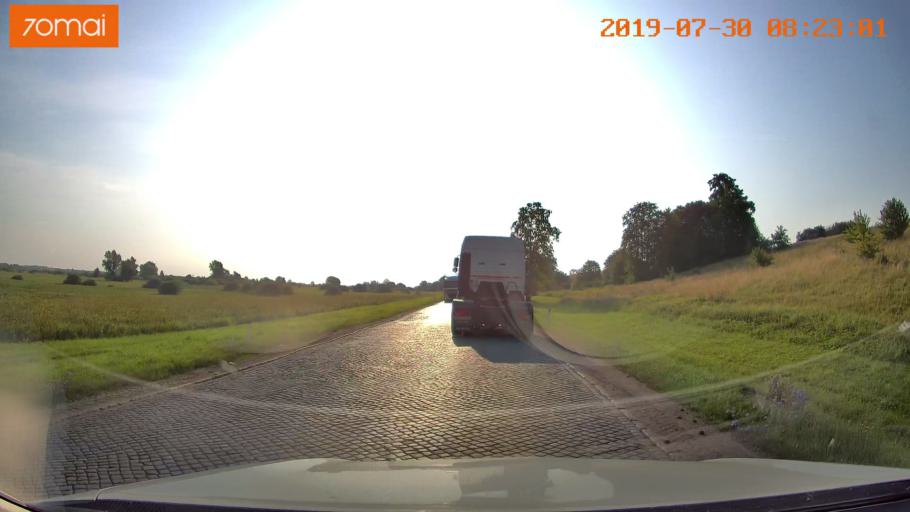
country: RU
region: Kaliningrad
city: Chernyakhovsk
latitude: 54.6251
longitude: 21.5382
